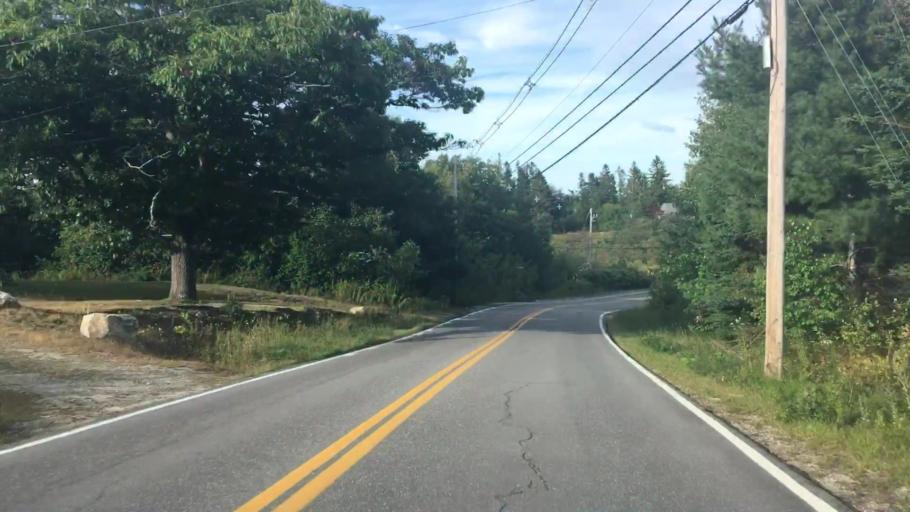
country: US
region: Maine
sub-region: Hancock County
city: Trenton
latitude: 44.4370
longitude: -68.3963
